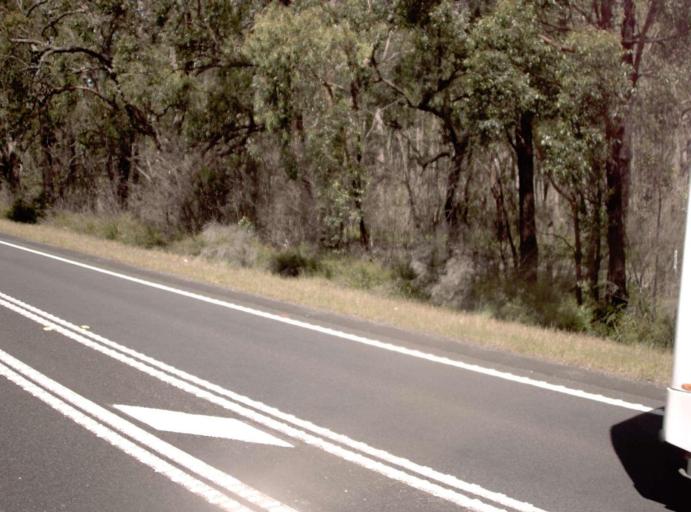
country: AU
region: Victoria
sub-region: Wellington
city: Sale
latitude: -37.9180
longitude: 147.2882
